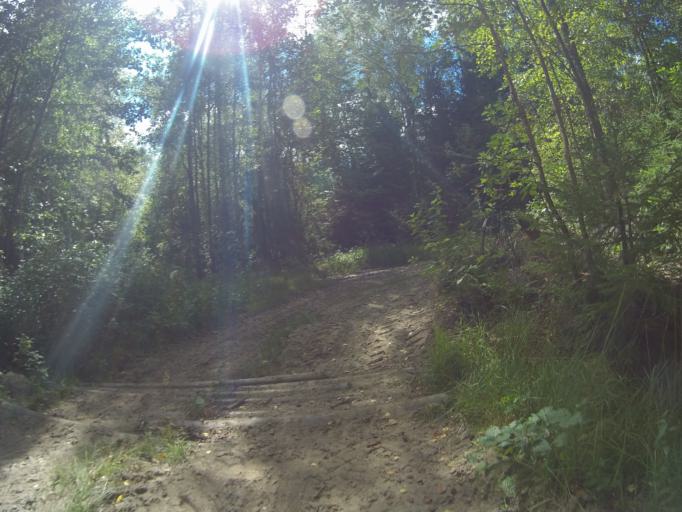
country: RU
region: Vladimir
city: Sobinka
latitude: 55.8665
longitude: 40.1582
